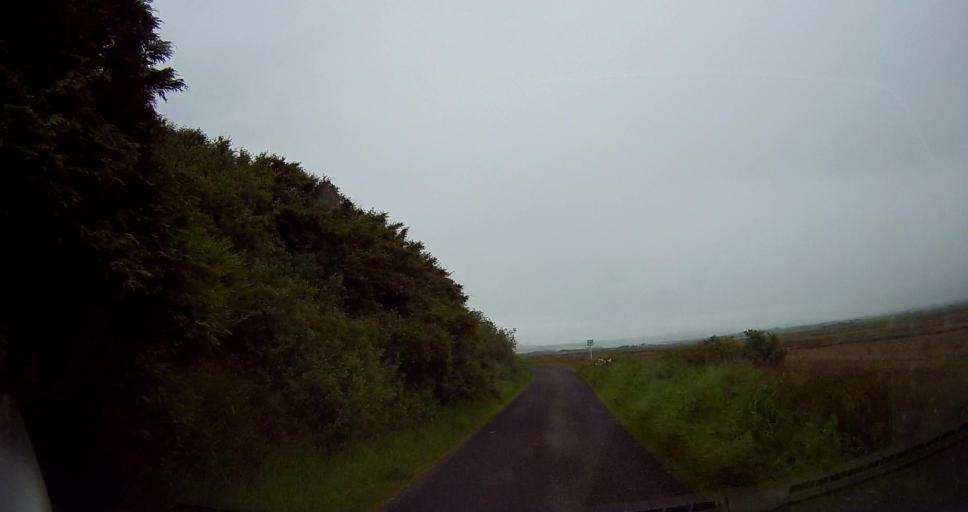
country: GB
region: Scotland
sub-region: Orkney Islands
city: Stromness
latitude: 58.9767
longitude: -3.1645
